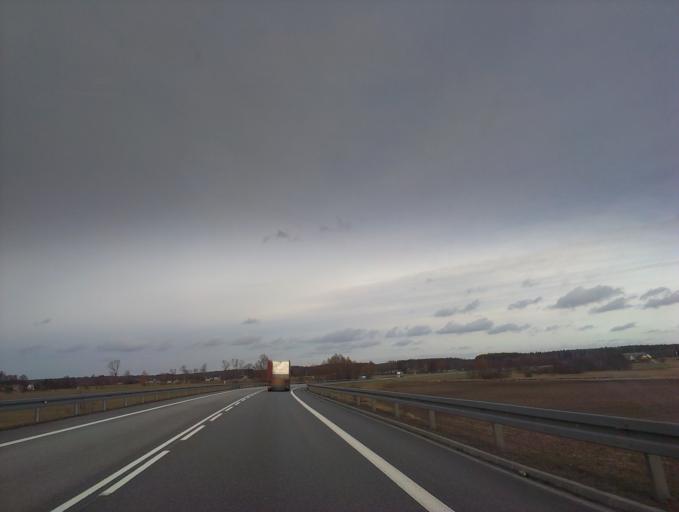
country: PL
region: Kujawsko-Pomorskie
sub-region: Powiat lipnowski
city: Skepe
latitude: 52.8721
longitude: 19.3172
